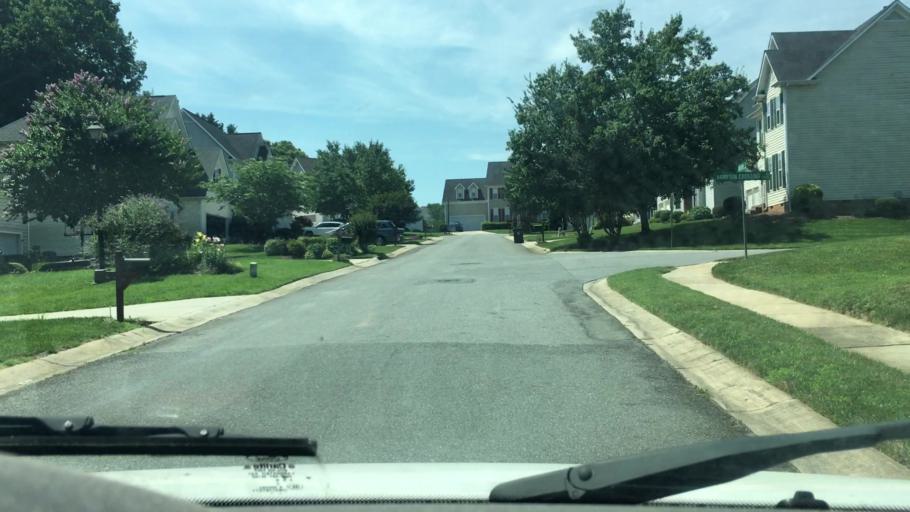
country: US
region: North Carolina
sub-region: Mecklenburg County
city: Huntersville
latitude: 35.4449
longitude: -80.8505
